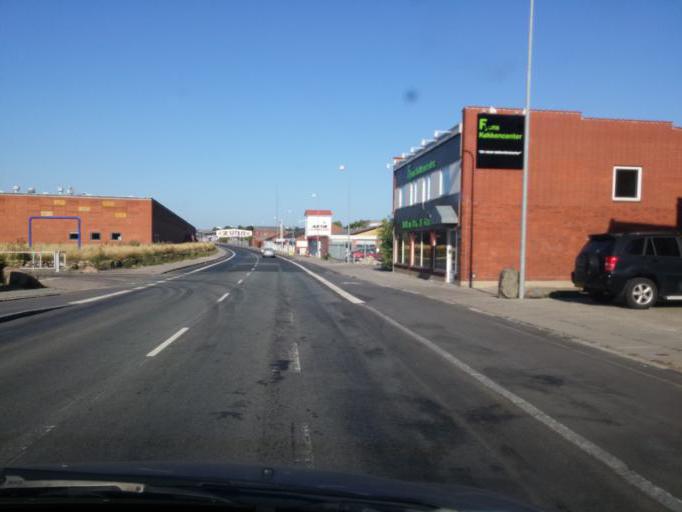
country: DK
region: South Denmark
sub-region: Odense Kommune
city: Odense
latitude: 55.4016
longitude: 10.4115
